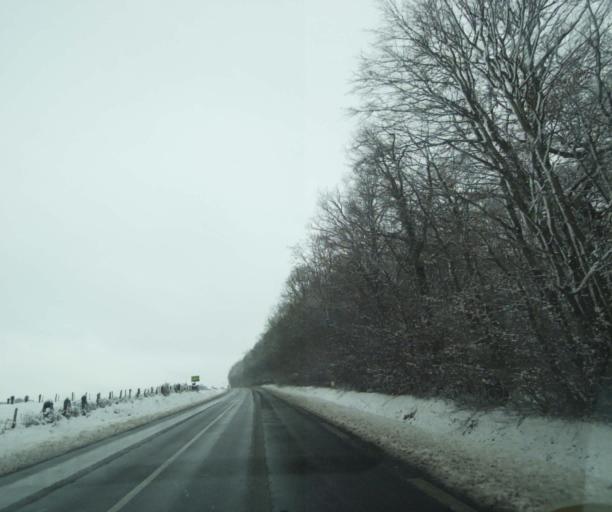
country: FR
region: Champagne-Ardenne
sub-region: Departement de la Haute-Marne
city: Montier-en-Der
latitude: 48.4877
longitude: 4.7755
